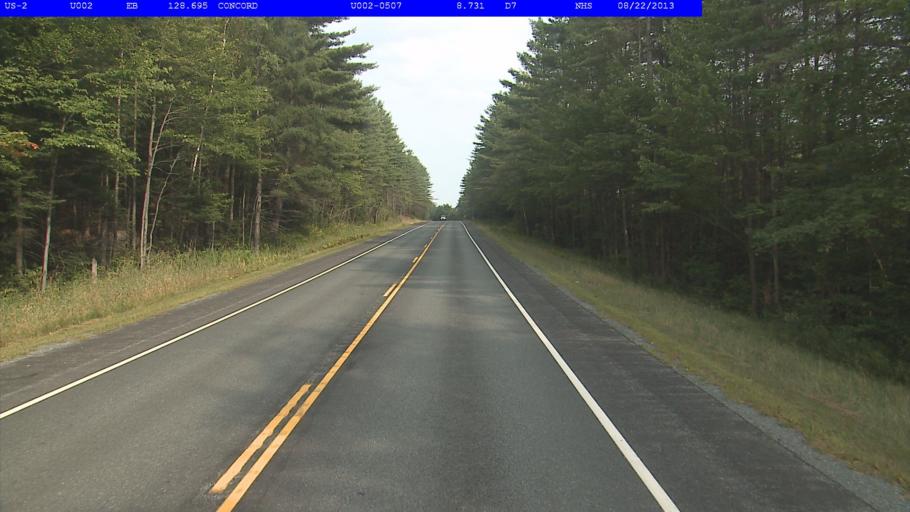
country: US
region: New Hampshire
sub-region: Grafton County
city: Littleton
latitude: 44.4506
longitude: -71.8018
